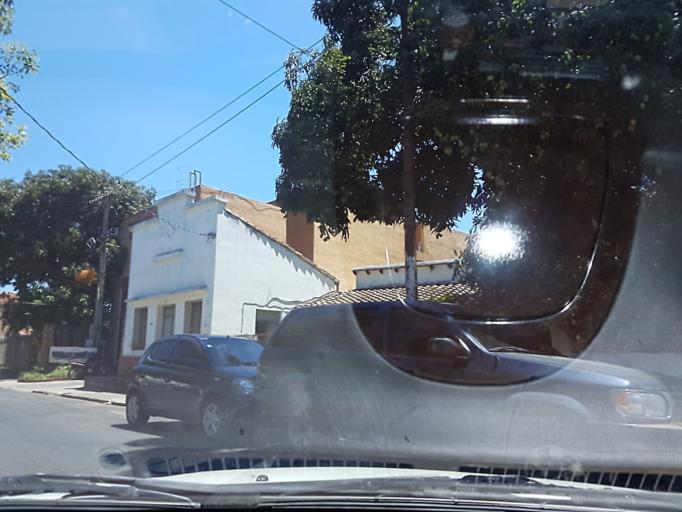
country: PY
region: Asuncion
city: Asuncion
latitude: -25.3073
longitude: -57.6038
